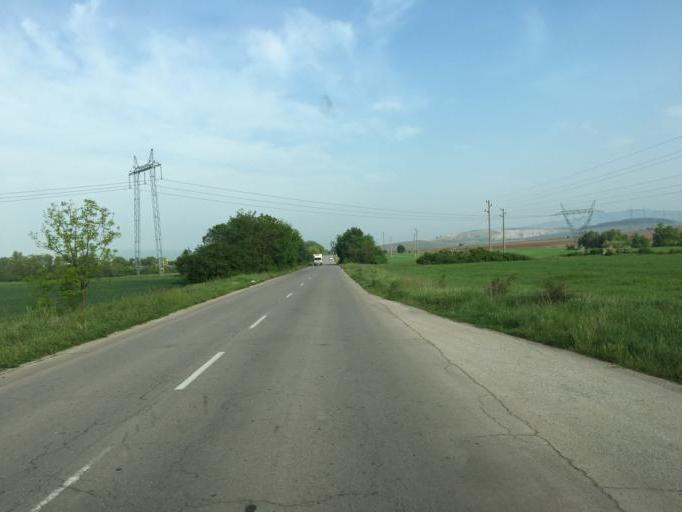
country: BG
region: Pernik
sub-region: Obshtina Radomir
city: Radomir
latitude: 42.4852
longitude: 23.0525
